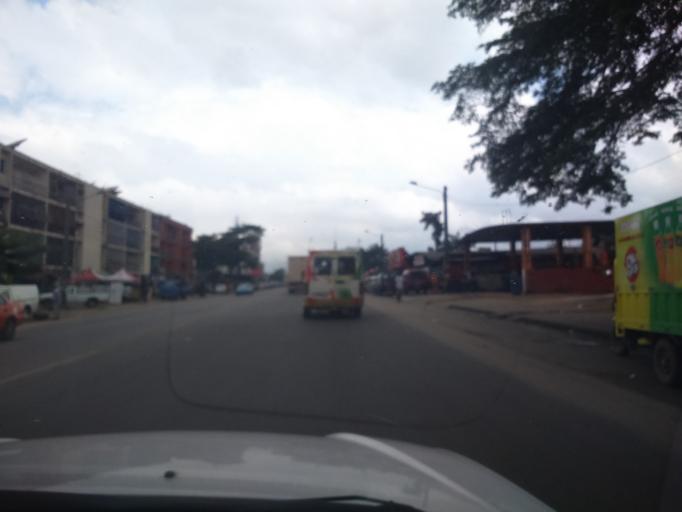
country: CI
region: Lagunes
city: Abidjan
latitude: 5.3482
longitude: -4.0634
